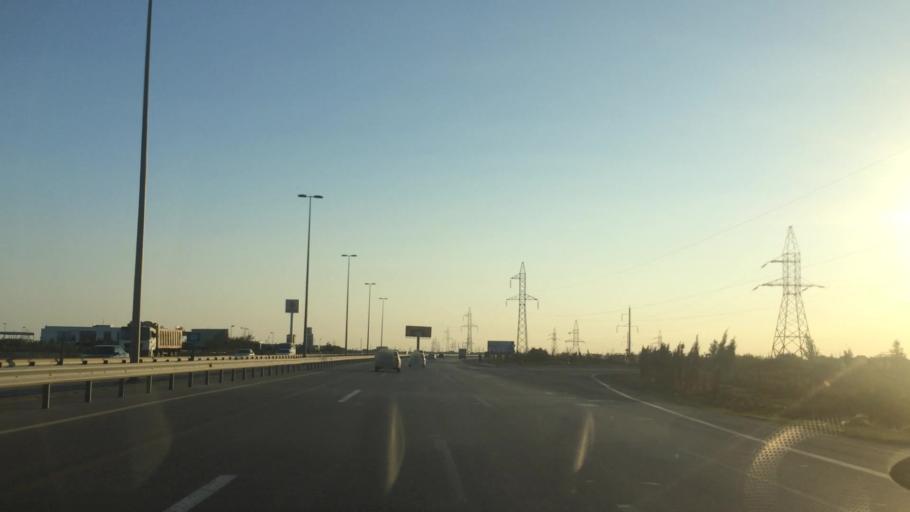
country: AZ
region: Baki
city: Qobustan
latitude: 39.9726
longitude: 49.4165
